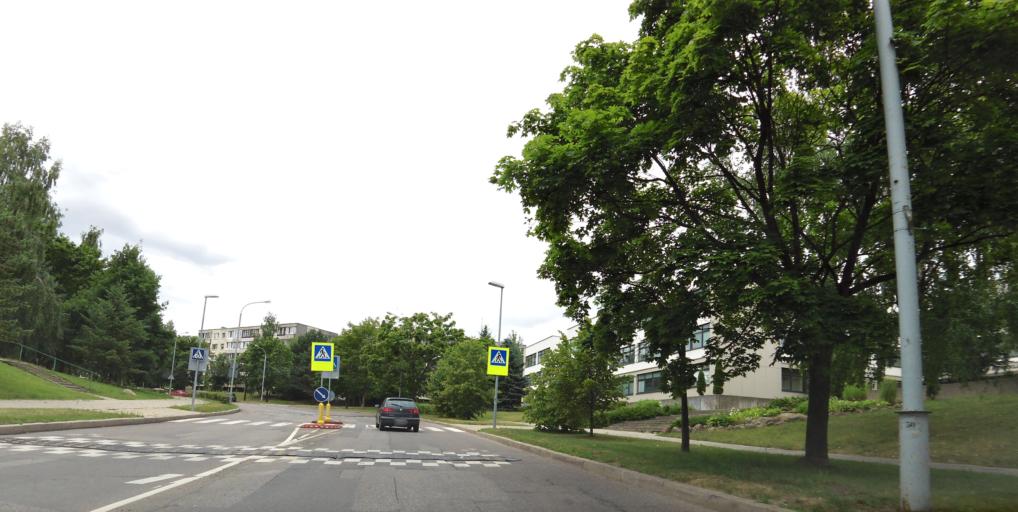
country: LT
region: Vilnius County
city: Justiniskes
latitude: 54.7125
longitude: 25.2266
